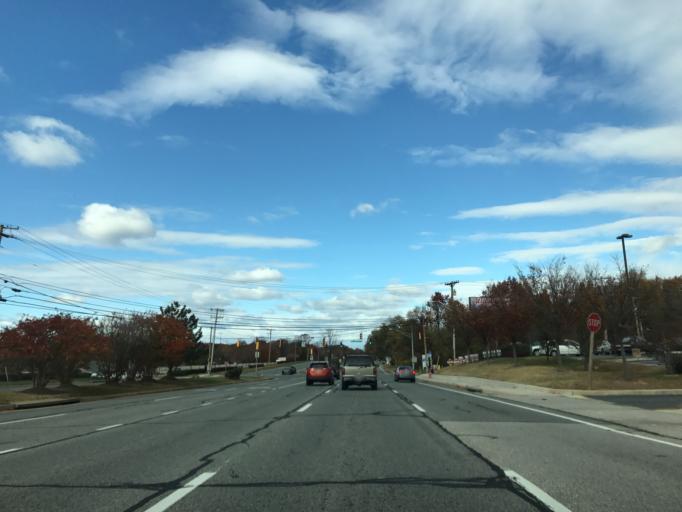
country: US
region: Maryland
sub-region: Anne Arundel County
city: South Gate
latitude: 39.1400
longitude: -76.6021
